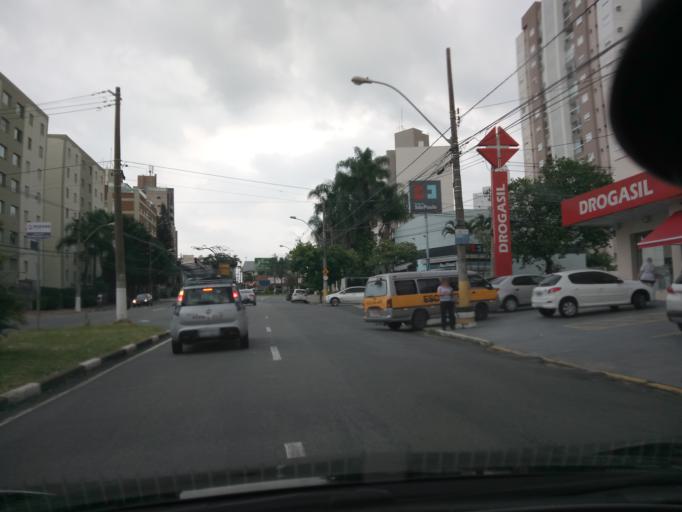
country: BR
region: Sao Paulo
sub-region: Campinas
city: Campinas
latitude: -22.8887
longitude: -47.0325
